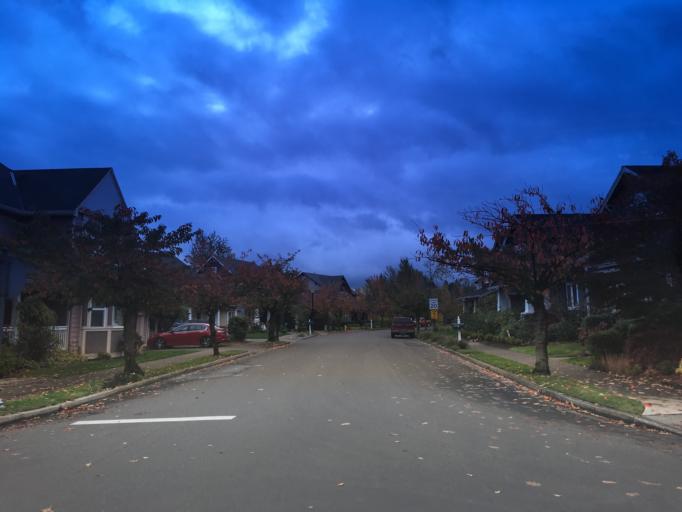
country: US
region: Oregon
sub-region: Multnomah County
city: Fairview
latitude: 45.5310
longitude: -122.4374
